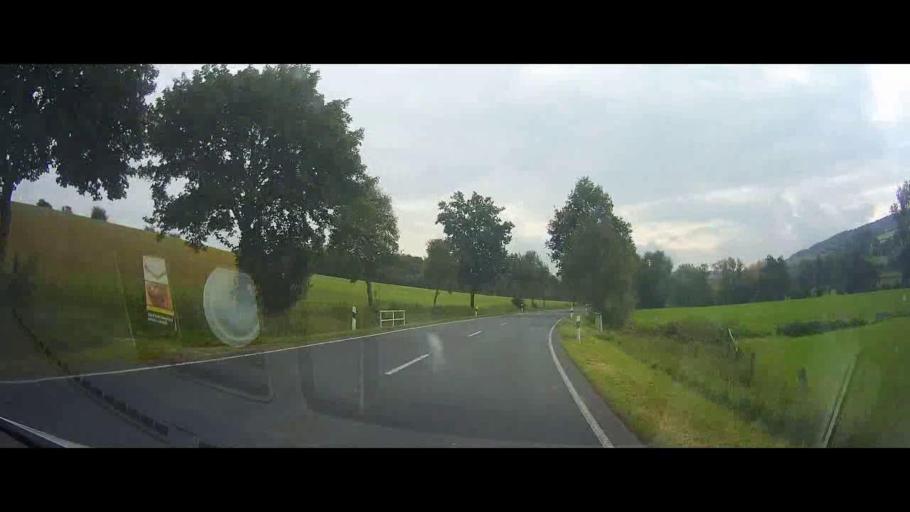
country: DE
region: Lower Saxony
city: Uslar
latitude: 51.6098
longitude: 9.6736
